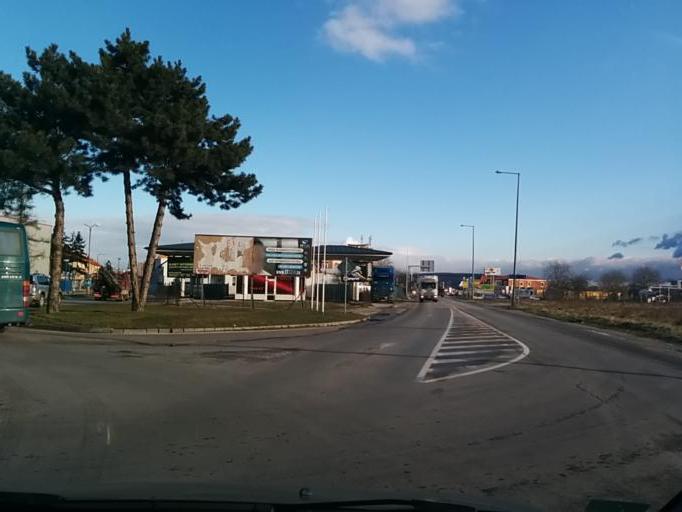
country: SK
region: Trenciansky
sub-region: Okres Nove Mesto nad Vahom
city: Nove Mesto nad Vahom
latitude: 48.7444
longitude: 17.8377
